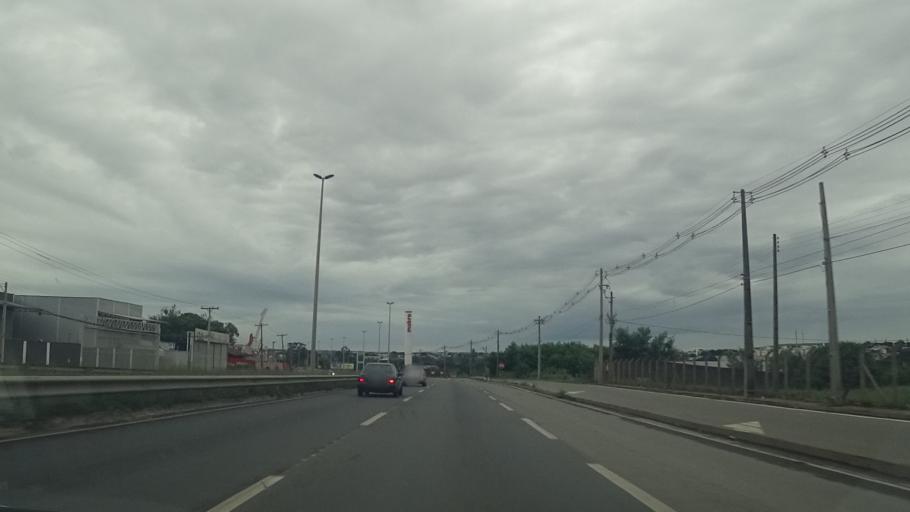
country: BR
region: Goias
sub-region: Goiania
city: Goiania
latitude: -16.7490
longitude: -49.2411
